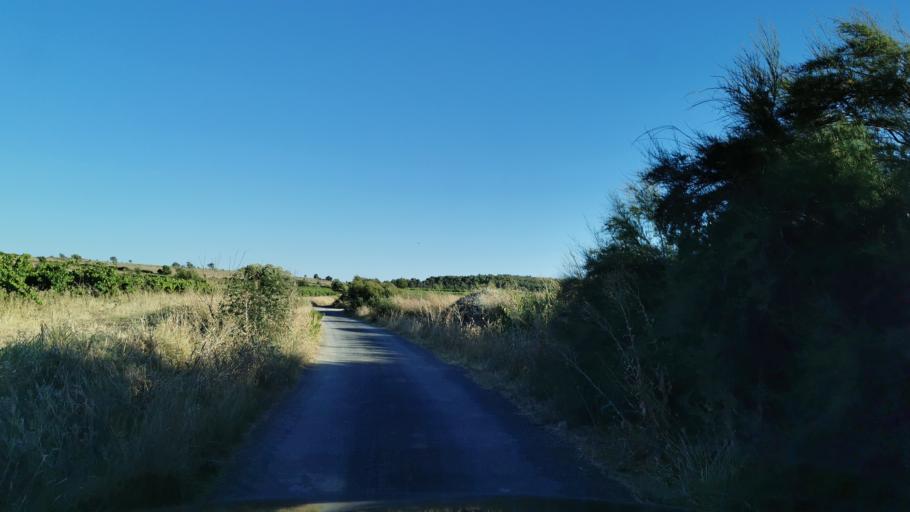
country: FR
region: Languedoc-Roussillon
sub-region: Departement de l'Aude
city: Ouveillan
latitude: 43.2785
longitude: 2.9762
